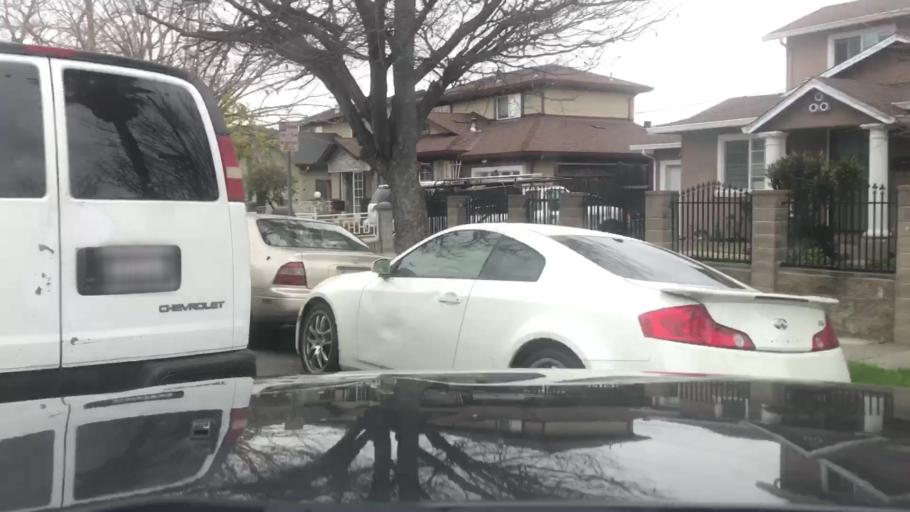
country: US
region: California
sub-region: Santa Clara County
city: Seven Trees
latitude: 37.3213
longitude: -121.8181
